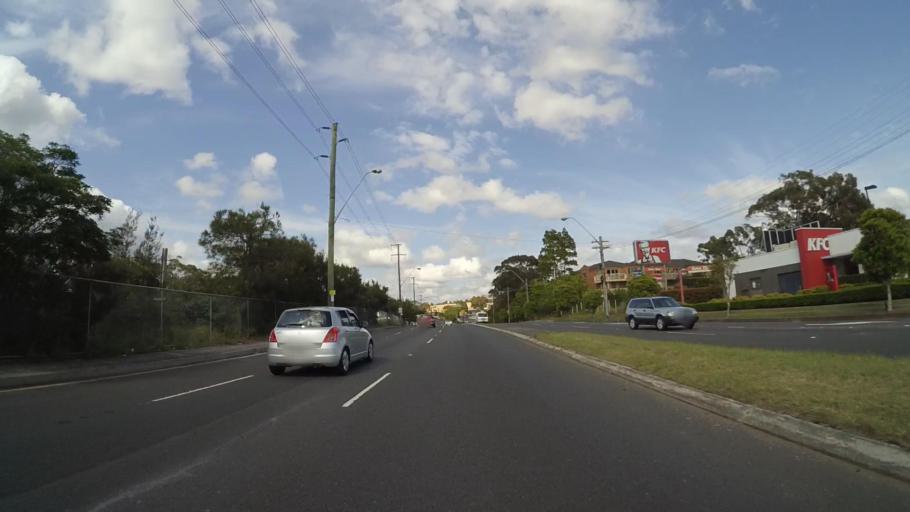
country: AU
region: New South Wales
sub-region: Sutherland Shire
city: Engadine
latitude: -34.0650
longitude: 151.0175
